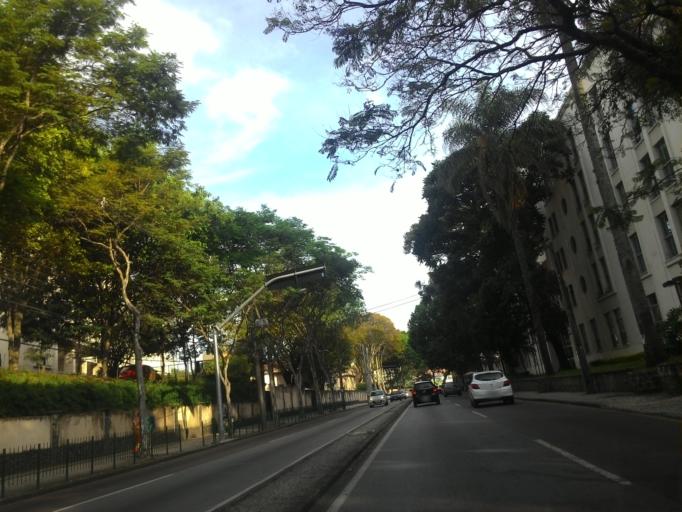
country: BR
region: Parana
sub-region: Curitiba
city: Curitiba
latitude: -25.4238
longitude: -49.2676
